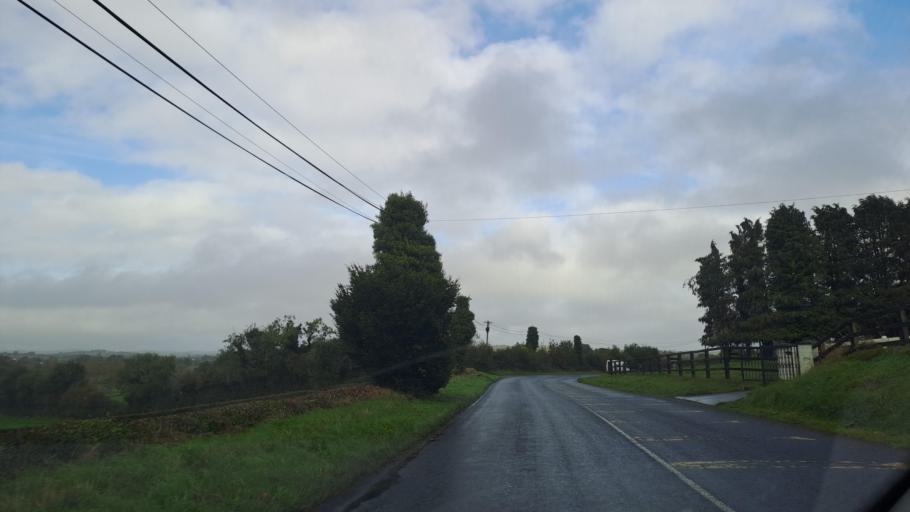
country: IE
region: Ulster
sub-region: County Monaghan
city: Carrickmacross
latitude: 53.9515
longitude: -6.7173
